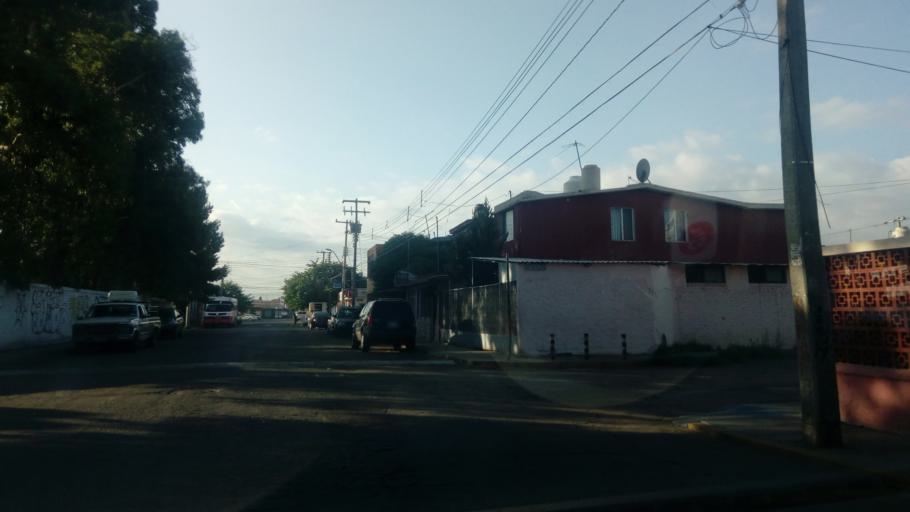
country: MX
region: Durango
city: Victoria de Durango
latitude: 24.0486
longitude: -104.6199
